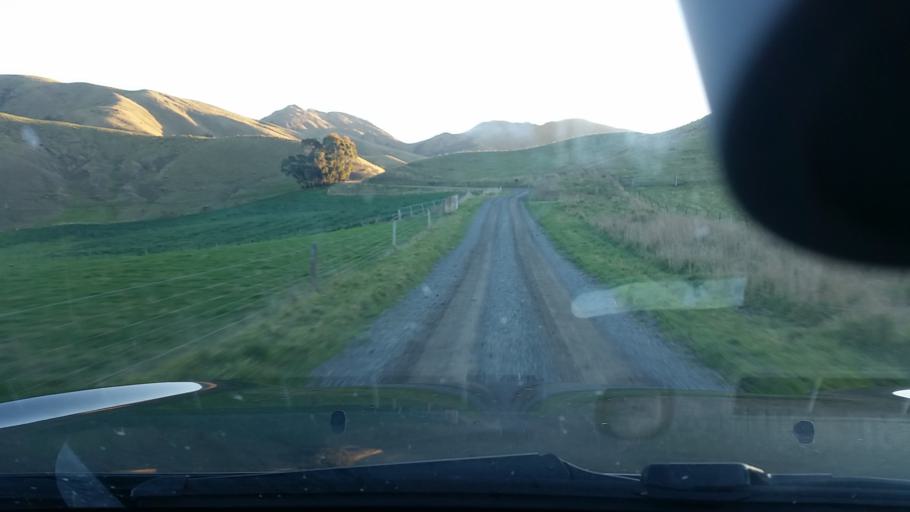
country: NZ
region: Marlborough
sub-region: Marlborough District
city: Blenheim
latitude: -41.7487
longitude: 174.0730
